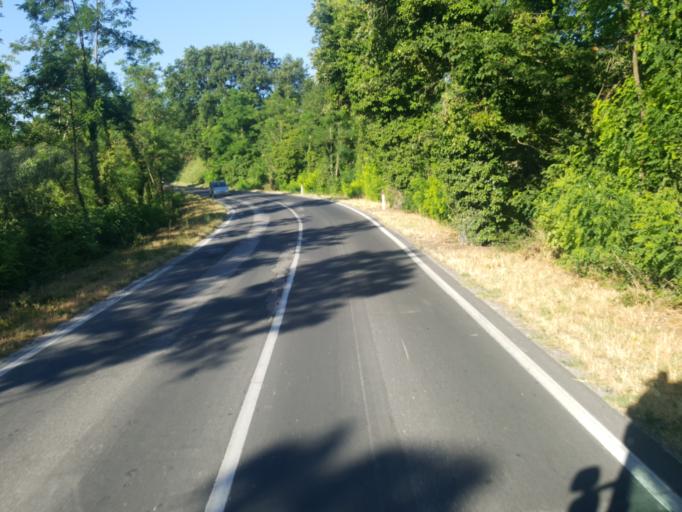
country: IT
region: The Marches
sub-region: Provincia di Pesaro e Urbino
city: Padiglione
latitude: 43.8440
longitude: 12.7109
